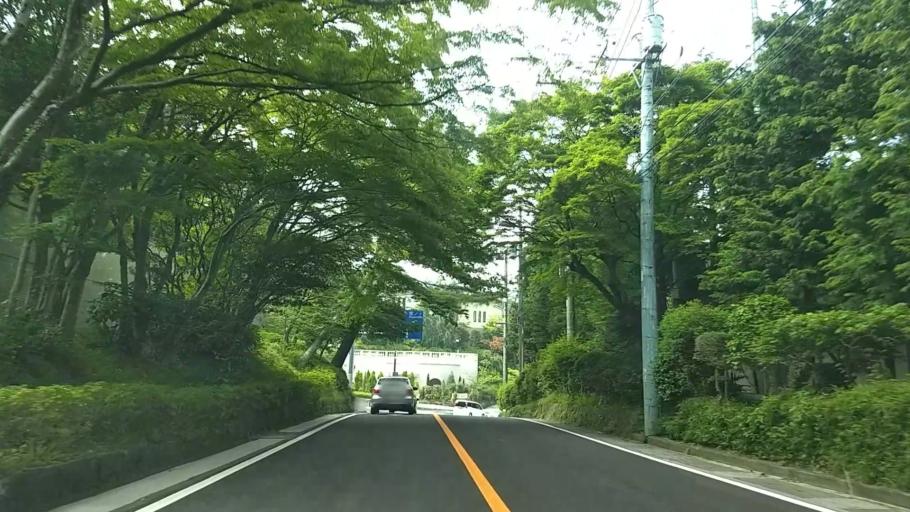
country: JP
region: Kanagawa
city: Hakone
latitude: 35.2381
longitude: 139.0467
